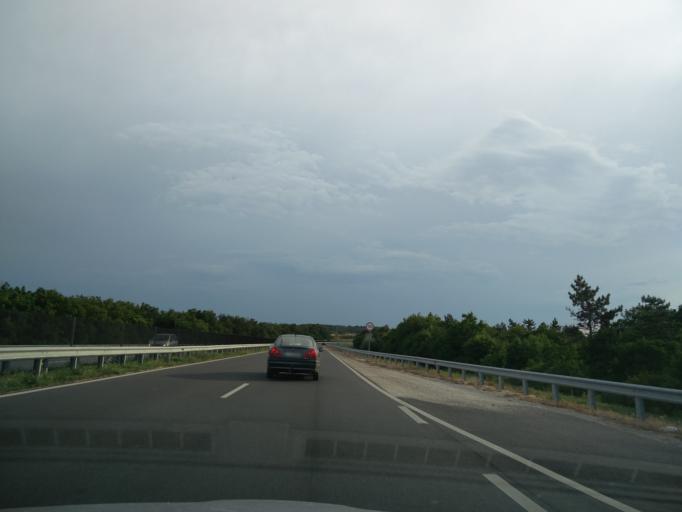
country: HU
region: Veszprem
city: Petfuerdo
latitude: 47.1508
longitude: 18.0729
